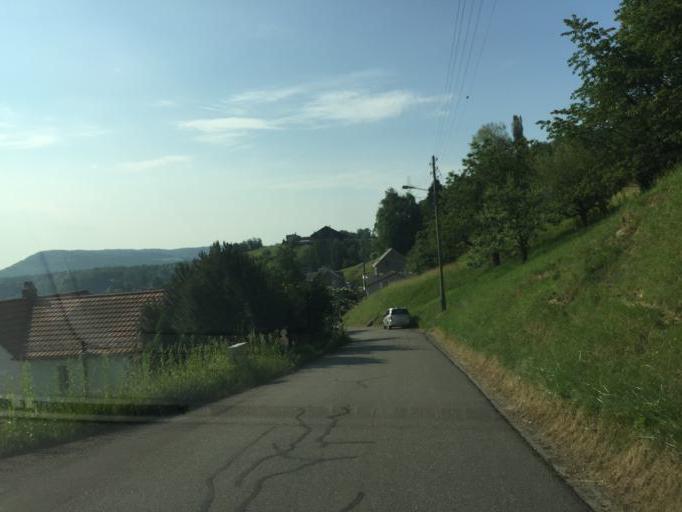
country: CH
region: Zurich
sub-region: Bezirk Buelach
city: Rorbas
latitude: 47.5336
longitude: 8.5681
